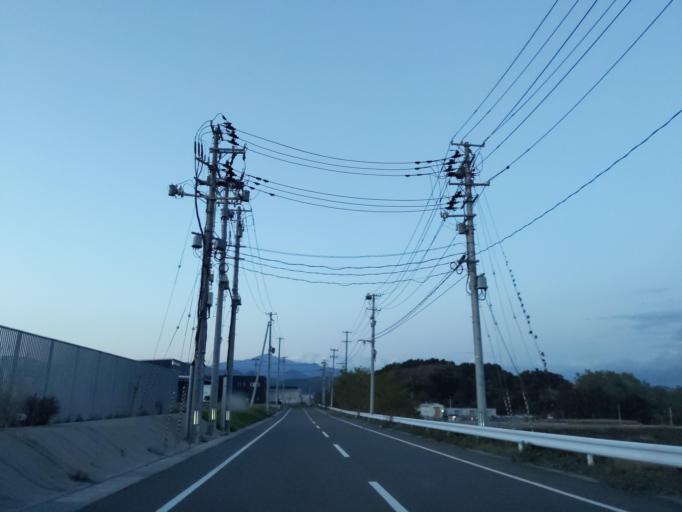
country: JP
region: Fukushima
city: Koriyama
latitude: 37.4588
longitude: 140.3043
